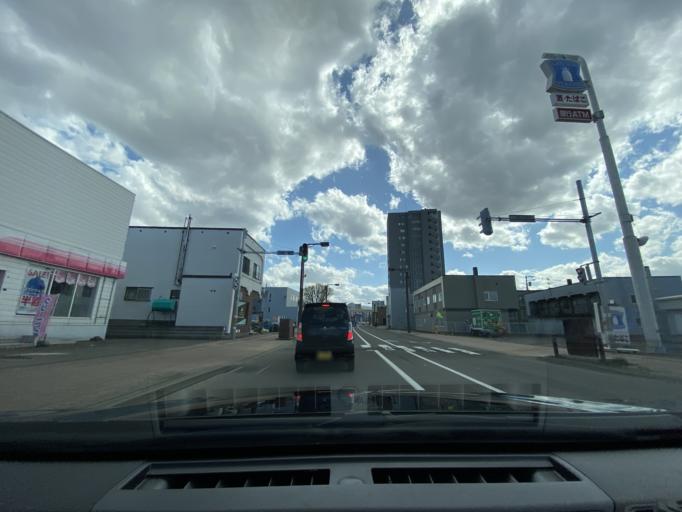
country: JP
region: Hokkaido
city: Sapporo
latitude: 43.0890
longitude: 141.3172
